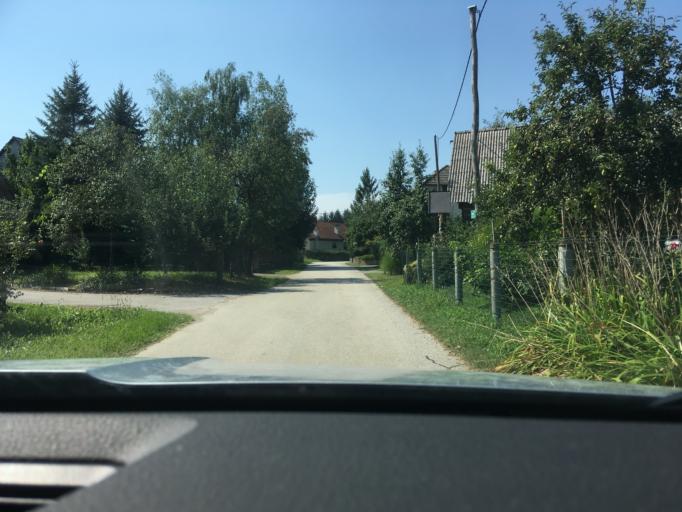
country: SI
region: Metlika
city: Metlika
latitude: 45.6146
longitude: 15.2959
